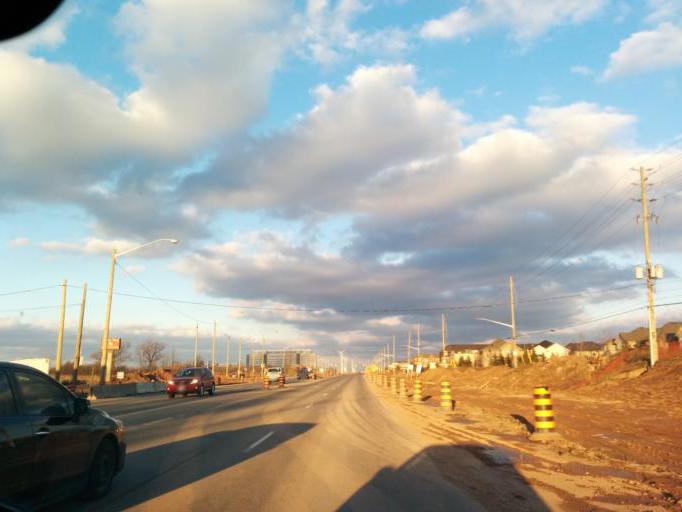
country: CA
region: Ontario
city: Burlington
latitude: 43.4397
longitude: -79.7722
